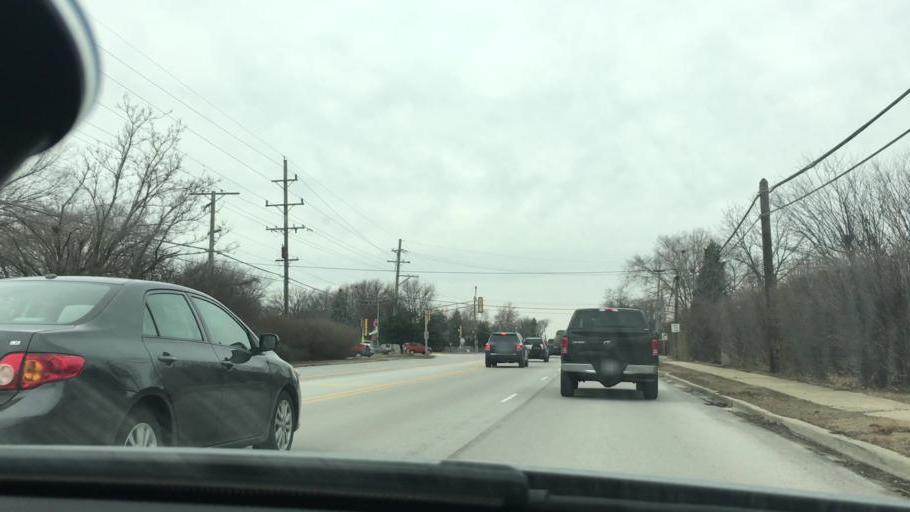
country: US
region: Illinois
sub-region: Cook County
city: Mount Prospect
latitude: 42.0601
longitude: -87.9088
